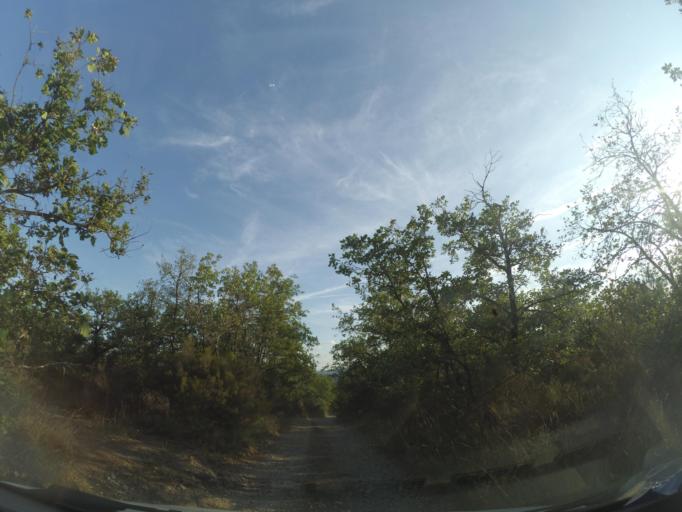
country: IT
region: Tuscany
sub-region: Province of Arezzo
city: Castiglion Fibocchi
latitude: 43.5340
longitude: 11.7859
